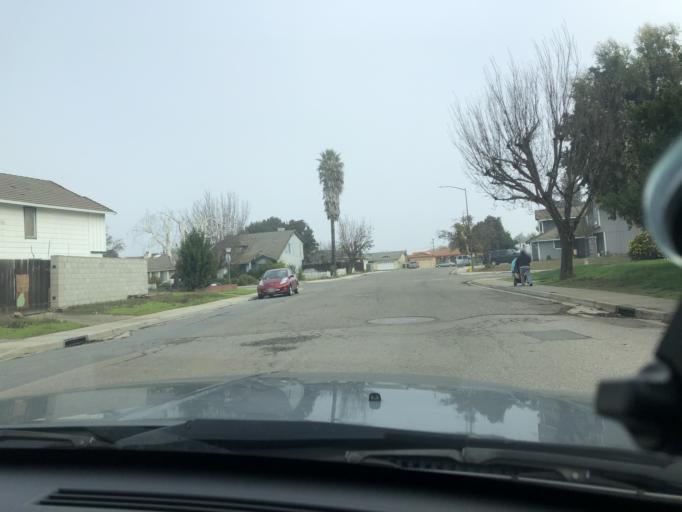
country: US
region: California
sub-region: Monterey County
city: King City
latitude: 36.2124
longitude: -121.1359
